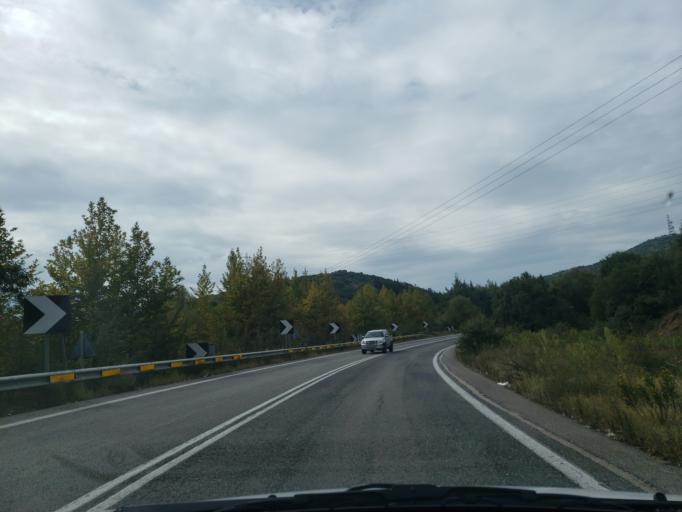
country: GR
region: Central Greece
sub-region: Nomos Fthiotidos
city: Stavros
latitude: 39.0020
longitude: 22.3736
